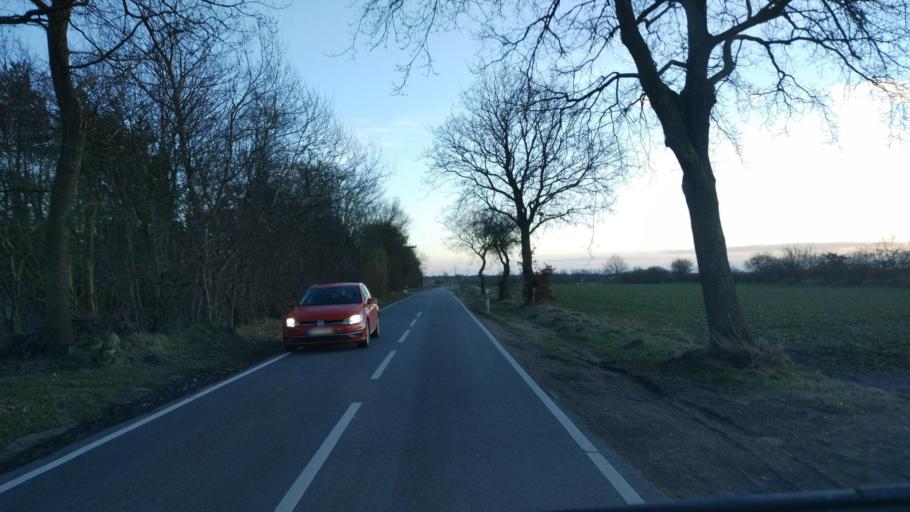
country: DE
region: Schleswig-Holstein
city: Ellingstedt
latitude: 54.4699
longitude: 9.4116
